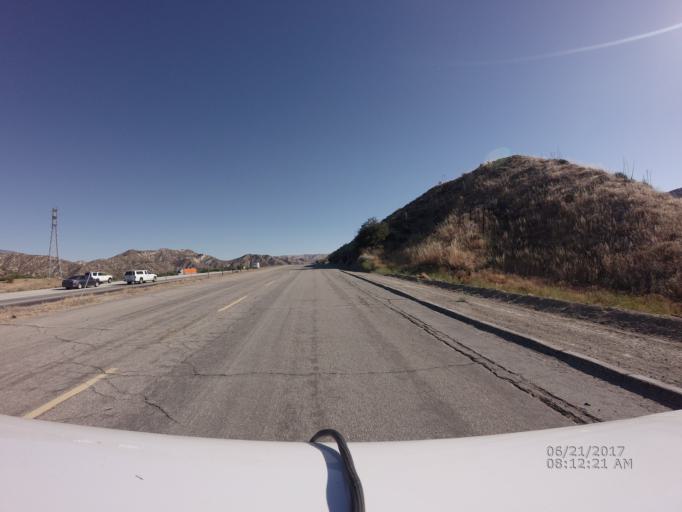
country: US
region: California
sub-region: Kern County
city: Lebec
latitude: 34.7167
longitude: -118.7982
